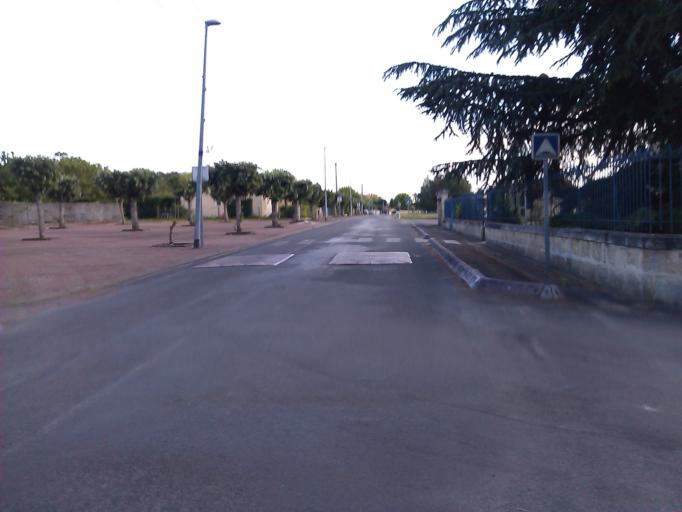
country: FR
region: Aquitaine
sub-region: Departement de la Gironde
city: Peujard
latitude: 45.0274
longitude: -0.4410
